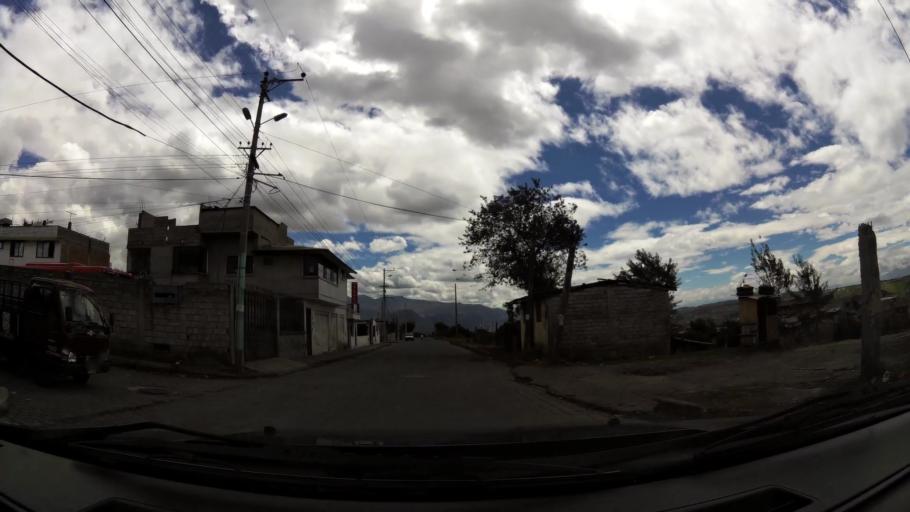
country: EC
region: Pichincha
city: Sangolqui
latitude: -0.3381
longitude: -78.5553
